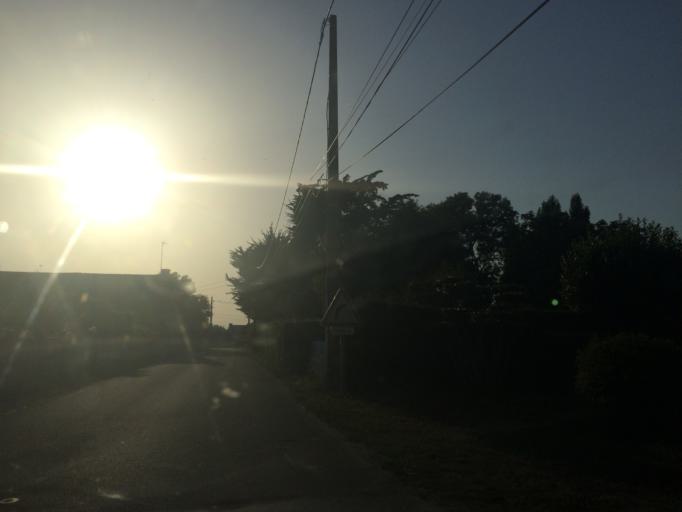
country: FR
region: Brittany
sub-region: Departement du Morbihan
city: Damgan
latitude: 47.5173
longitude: -2.5515
